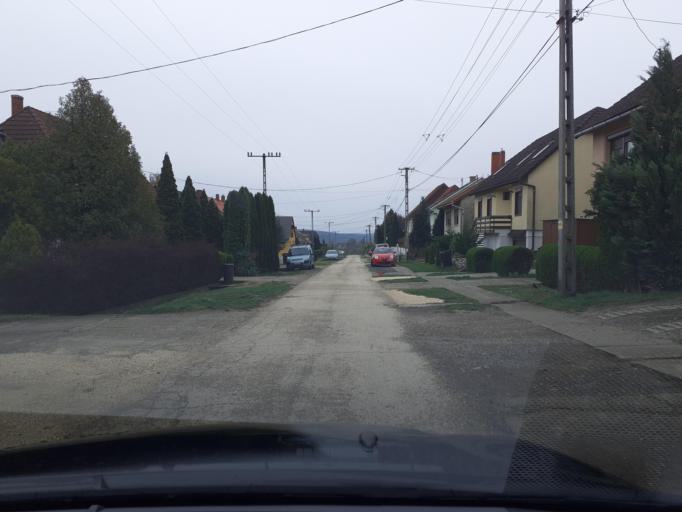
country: HU
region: Tolna
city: Hogyesz
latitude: 46.5002
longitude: 18.4110
